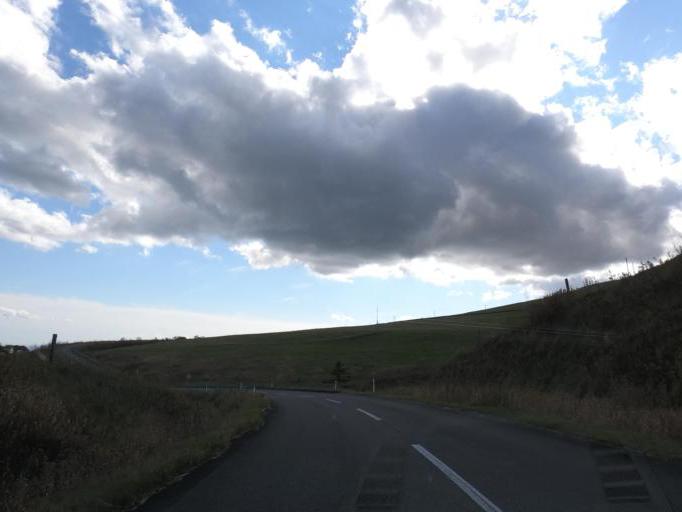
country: JP
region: Hokkaido
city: Otofuke
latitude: 43.2912
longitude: 143.1855
